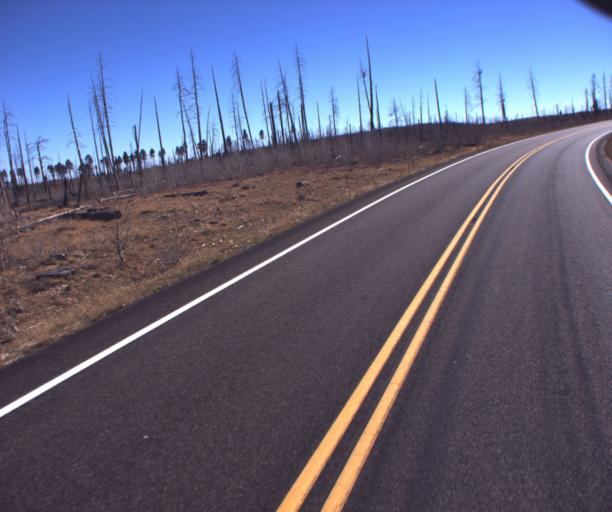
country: US
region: Arizona
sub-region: Coconino County
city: Fredonia
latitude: 36.5706
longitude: -112.1741
